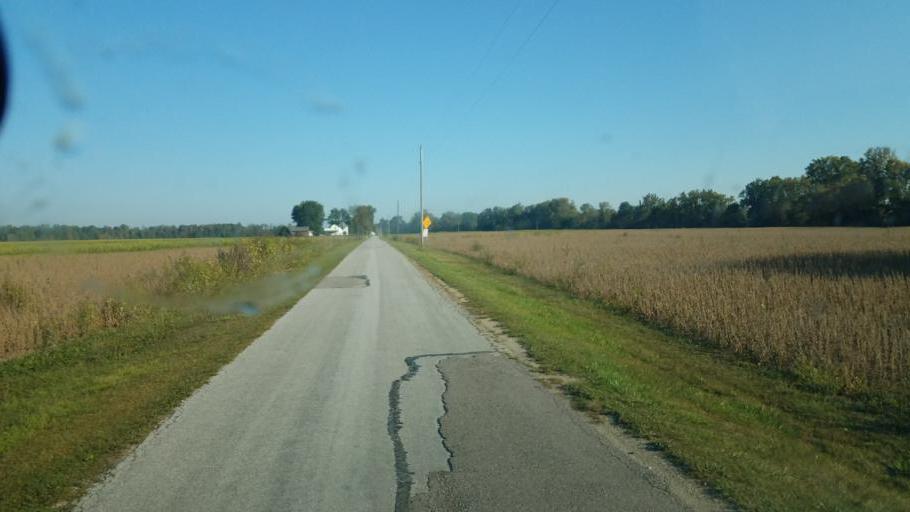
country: US
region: Ohio
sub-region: Union County
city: Richwood
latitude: 40.5457
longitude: -83.2678
